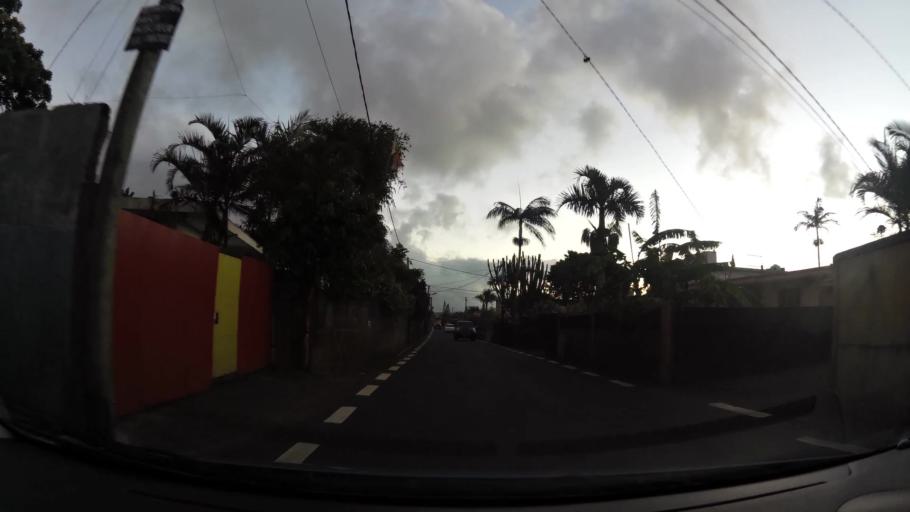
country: MU
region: Plaines Wilhems
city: Curepipe
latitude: -20.2901
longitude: 57.5239
